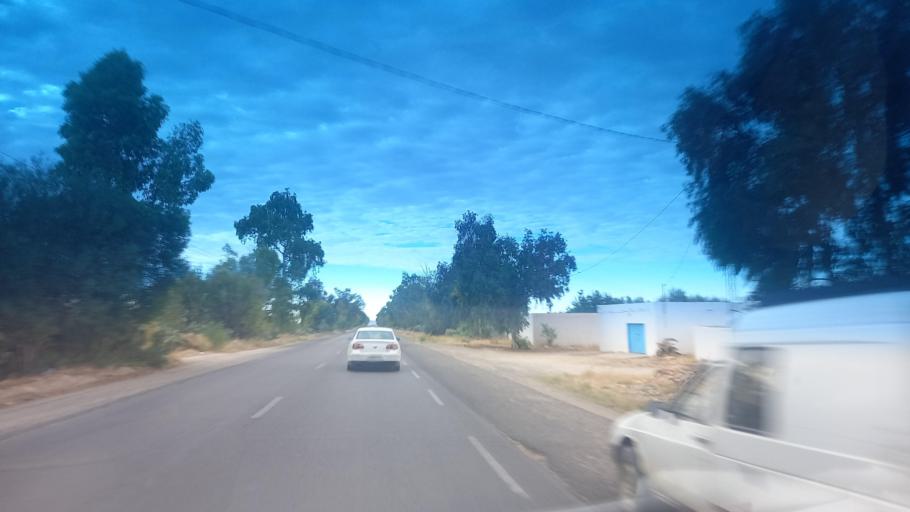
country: TN
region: Al Qasrayn
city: Sbiba
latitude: 35.2961
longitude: 9.0898
